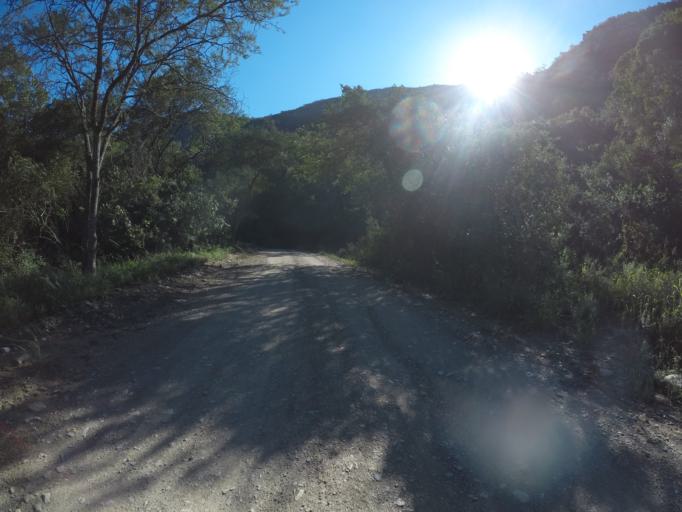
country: ZA
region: Eastern Cape
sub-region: Cacadu District Municipality
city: Kareedouw
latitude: -33.6599
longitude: 24.5351
